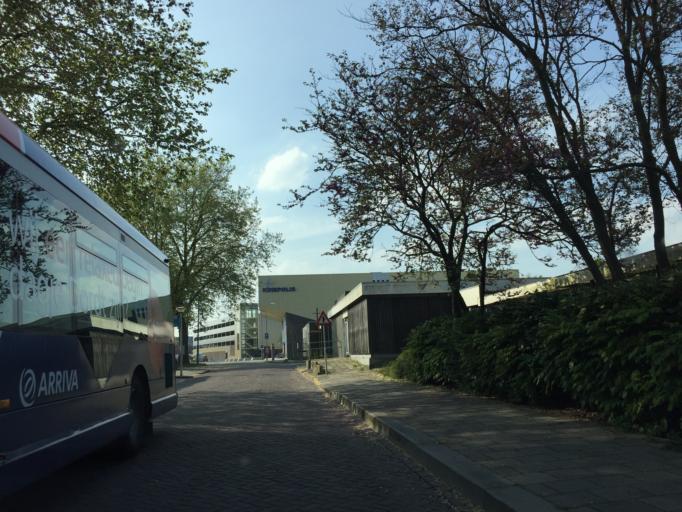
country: NL
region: South Holland
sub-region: Gemeente Dordrecht
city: Dordrecht
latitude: 51.8147
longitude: 4.6834
